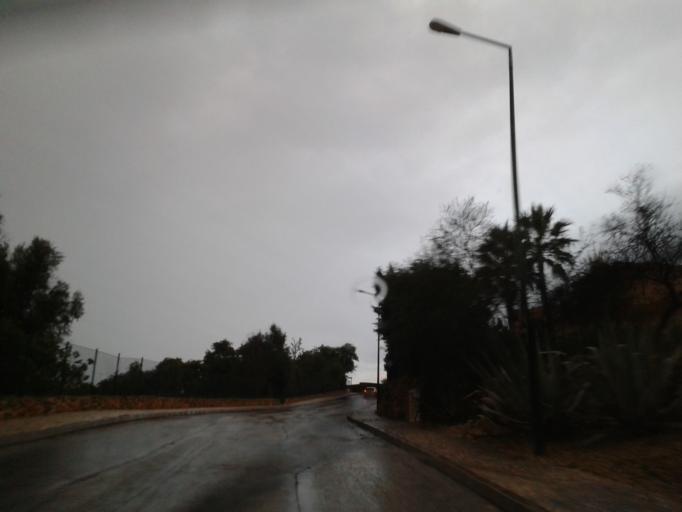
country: PT
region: Faro
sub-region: Lagoa
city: Estombar
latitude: 37.1309
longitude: -8.4858
